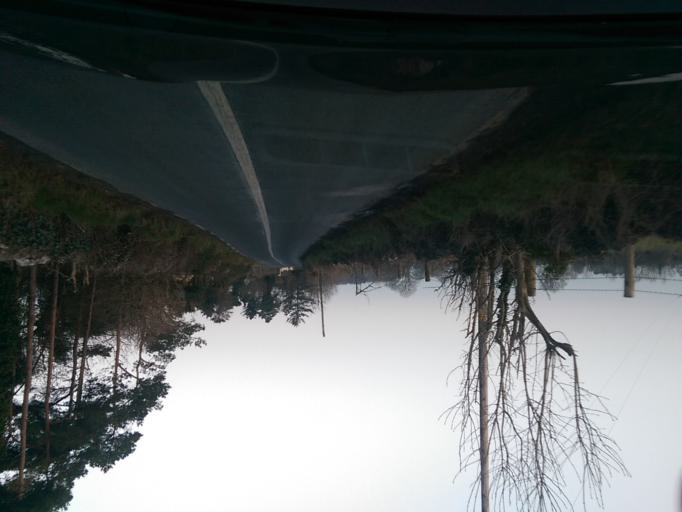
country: IE
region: Connaught
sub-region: County Galway
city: Athenry
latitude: 53.2379
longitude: -8.6624
